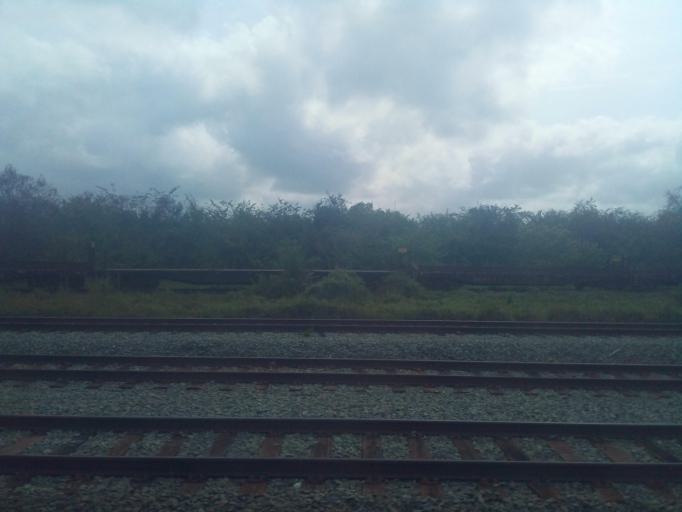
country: BR
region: Maranhao
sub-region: Icatu
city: Icatu
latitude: -2.9205
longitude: -44.3523
